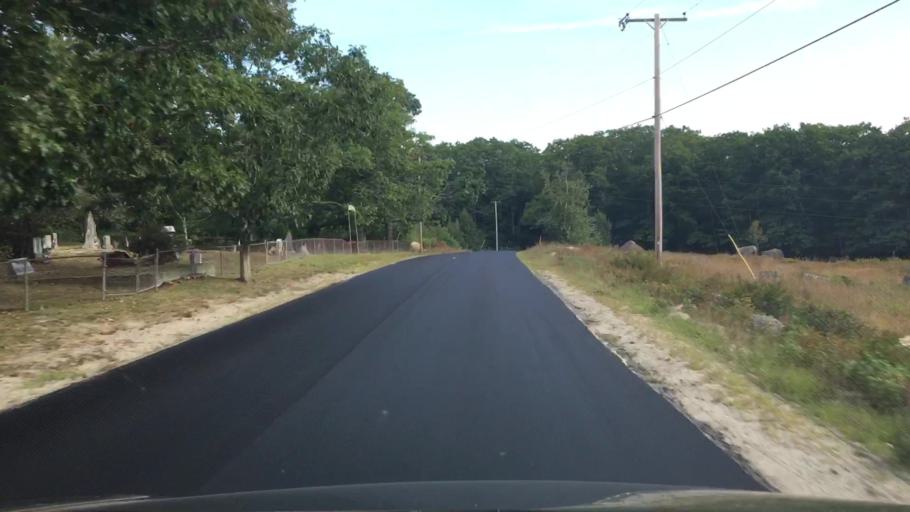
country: US
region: Maine
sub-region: Hancock County
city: Surry
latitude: 44.5267
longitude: -68.6102
